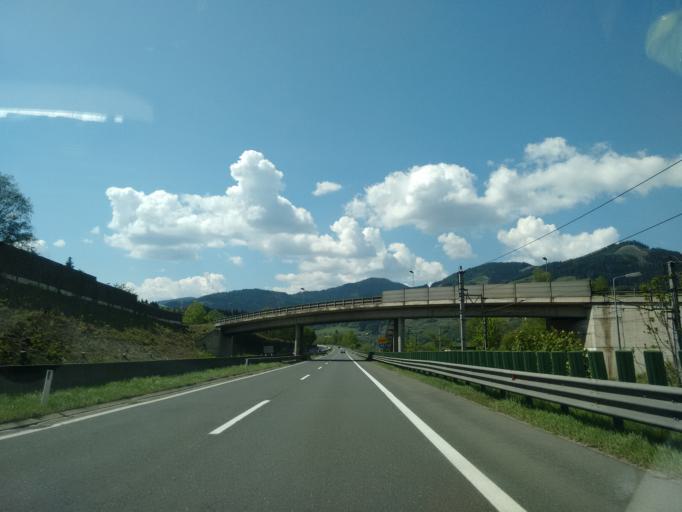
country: AT
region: Styria
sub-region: Politischer Bezirk Bruck-Muerzzuschlag
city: Oberaich
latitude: 47.4049
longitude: 15.2171
